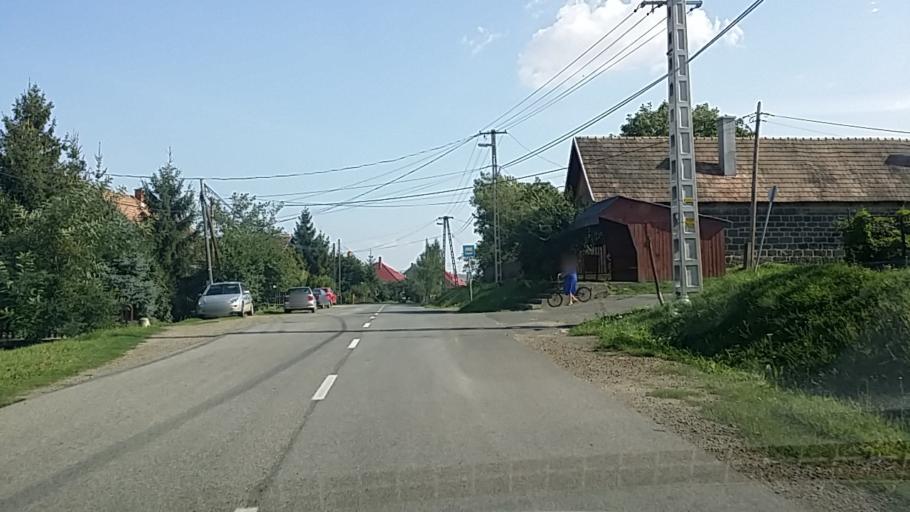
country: HU
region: Nograd
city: Bujak
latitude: 47.8799
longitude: 19.5539
